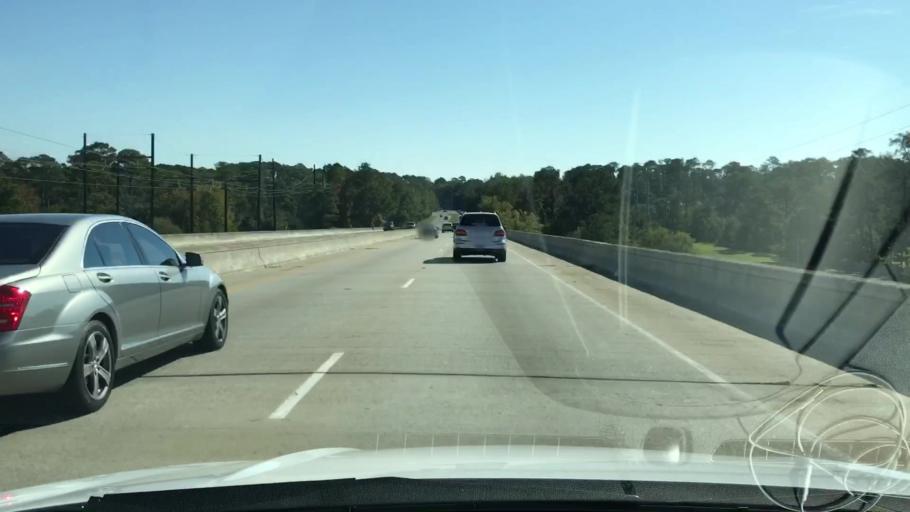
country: US
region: South Carolina
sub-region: Beaufort County
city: Hilton Head Island
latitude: 32.2232
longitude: -80.7804
